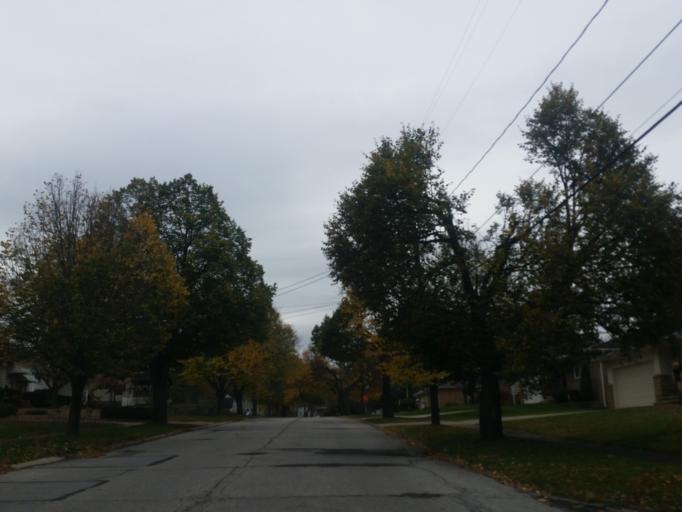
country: US
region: Ohio
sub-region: Cuyahoga County
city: Brooklyn Heights
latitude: 41.4277
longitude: -81.6875
